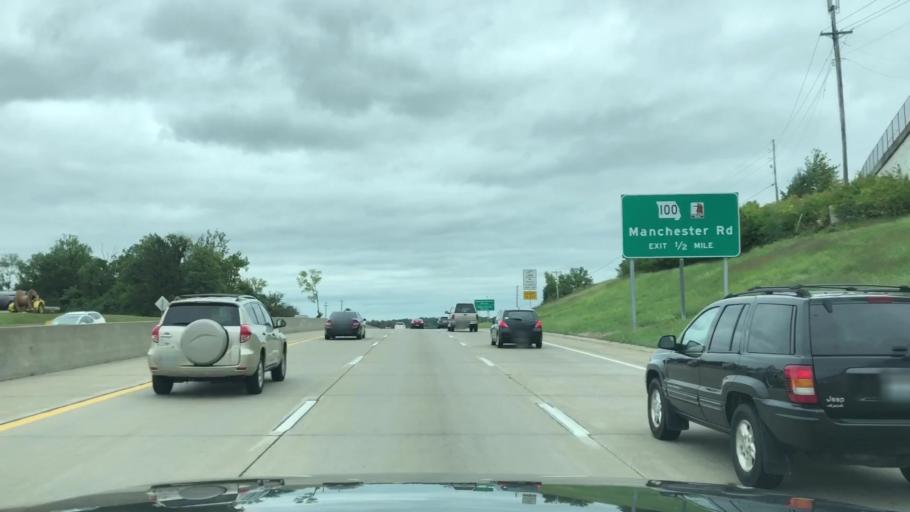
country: US
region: Missouri
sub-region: Saint Louis County
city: Manchester
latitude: 38.6021
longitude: -90.5100
